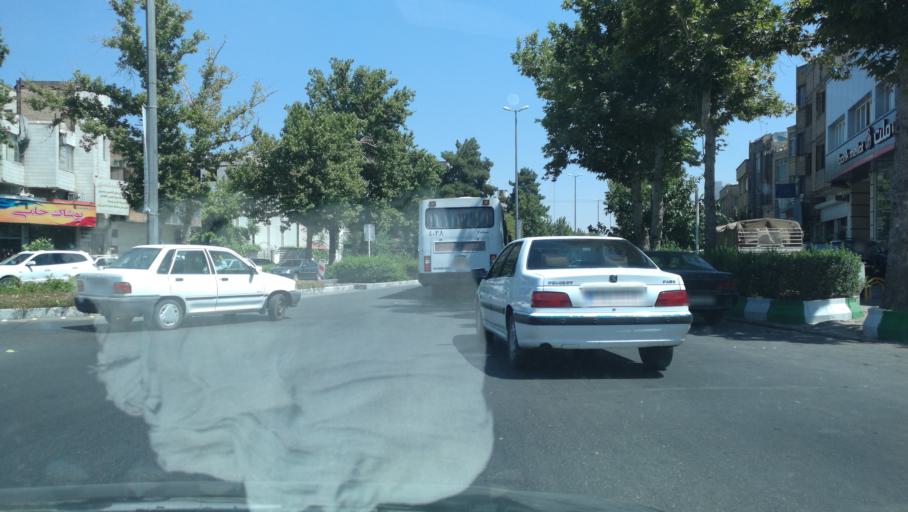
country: IR
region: Razavi Khorasan
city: Mashhad
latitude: 36.2742
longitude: 59.5924
